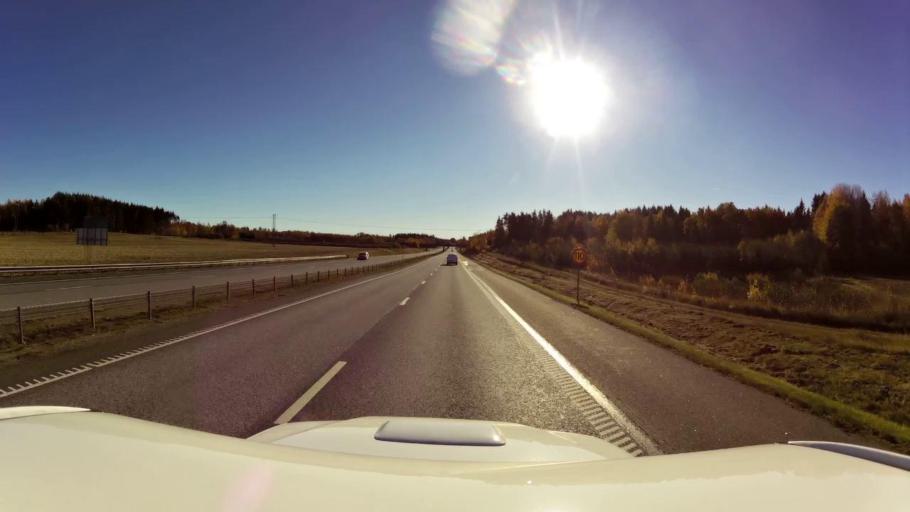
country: SE
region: OEstergoetland
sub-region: Linkopings Kommun
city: Malmslatt
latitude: 58.4182
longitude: 15.5421
